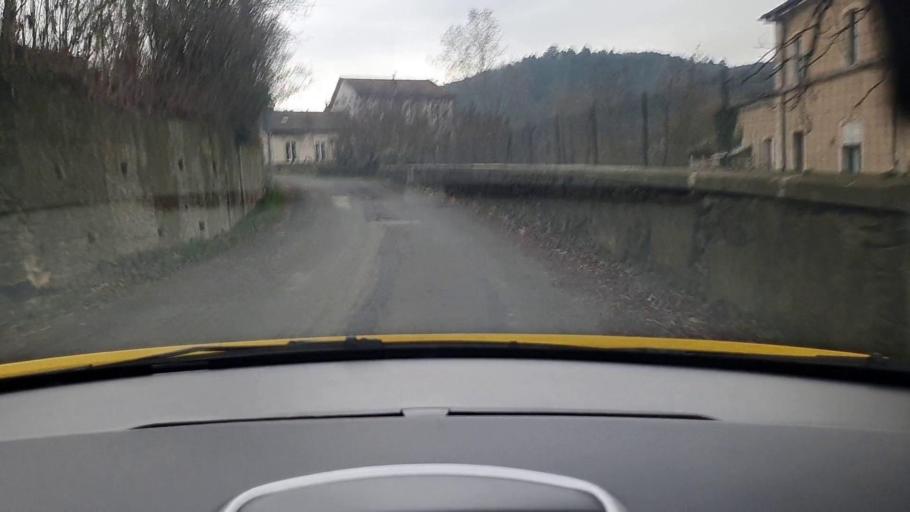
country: FR
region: Languedoc-Roussillon
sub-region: Departement du Gard
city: Besseges
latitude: 44.2763
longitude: 4.1232
